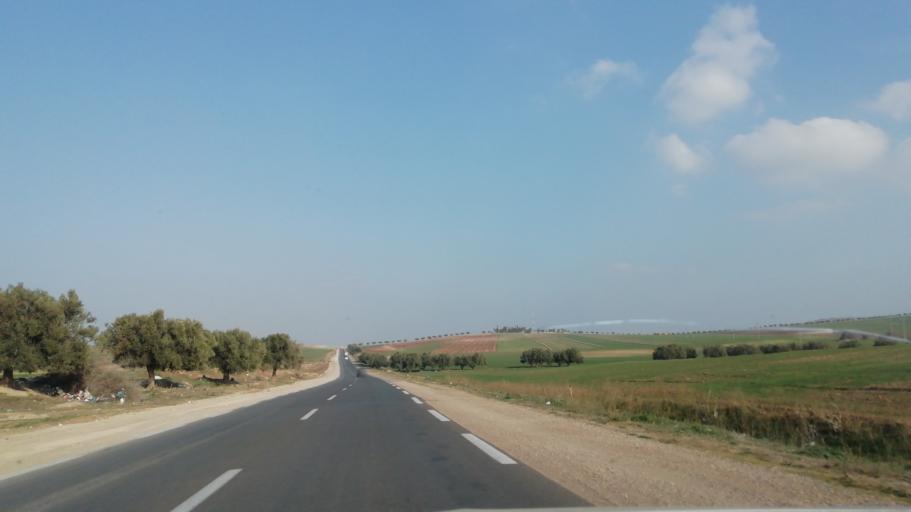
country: DZ
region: Ain Temouchent
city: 'Ain Temouchent
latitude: 35.2974
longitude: -1.0873
